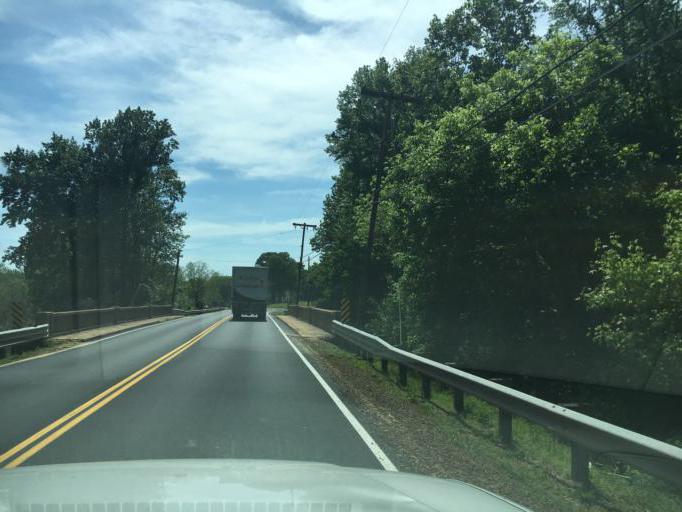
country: US
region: South Carolina
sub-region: Cherokee County
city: Blacksburg
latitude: 35.1246
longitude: -81.5090
